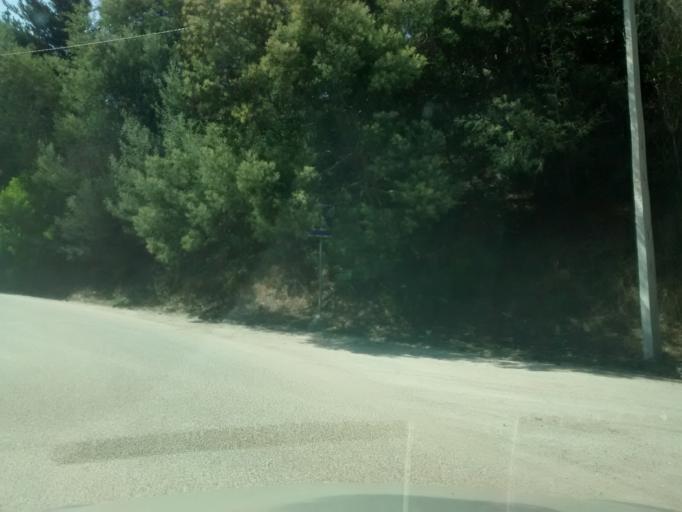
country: PT
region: Aveiro
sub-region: Mealhada
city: Mealhada
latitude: 40.3870
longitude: -8.3859
